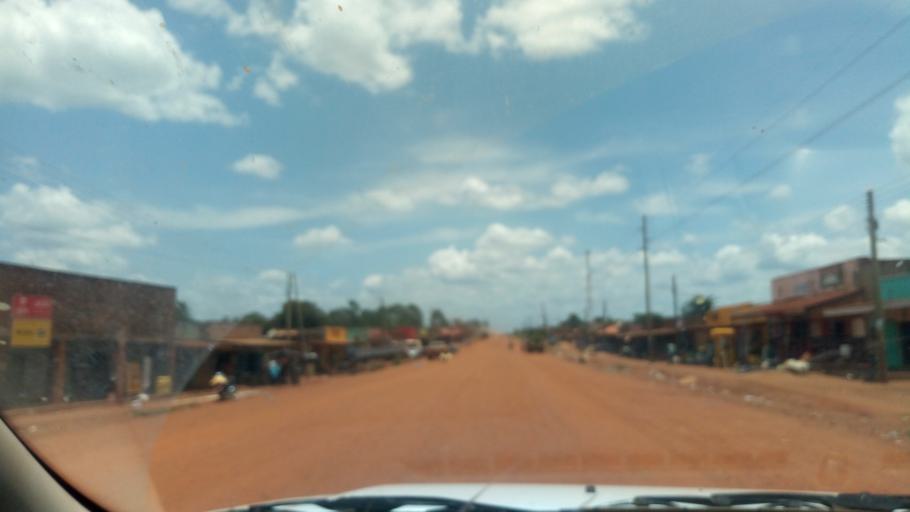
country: UG
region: Western Region
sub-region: Masindi District
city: Masindi
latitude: 1.7881
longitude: 31.8797
